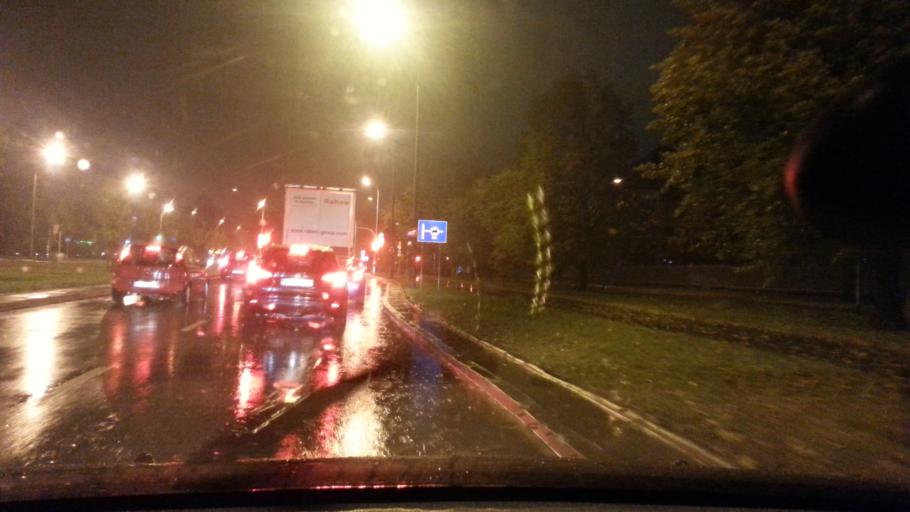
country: PL
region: Masovian Voivodeship
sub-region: Warszawa
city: Targowek
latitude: 52.2851
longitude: 21.0230
